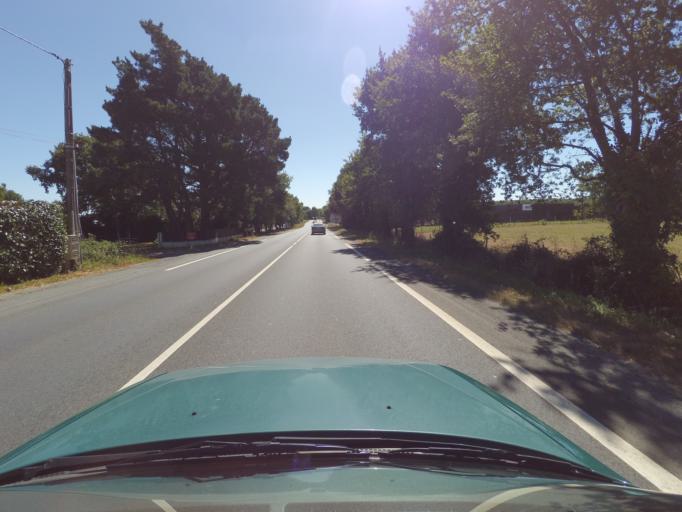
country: FR
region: Pays de la Loire
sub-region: Departement de la Loire-Atlantique
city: Aigrefeuille-sur-Maine
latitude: 47.0826
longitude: -1.4155
